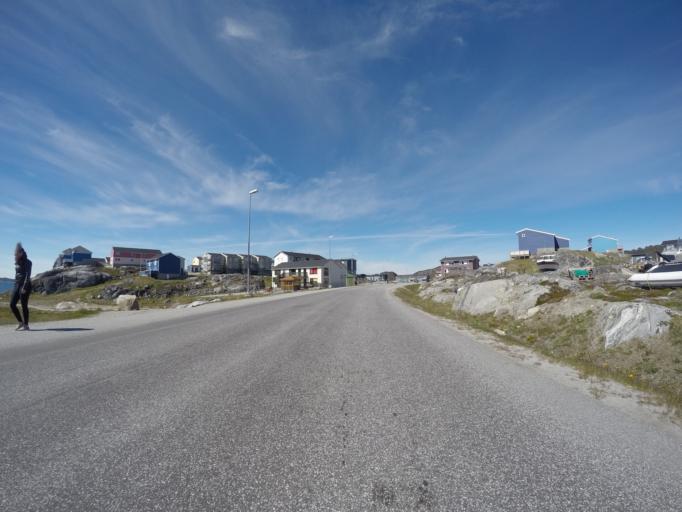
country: GL
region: Sermersooq
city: Nuuk
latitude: 64.1879
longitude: -51.7240
